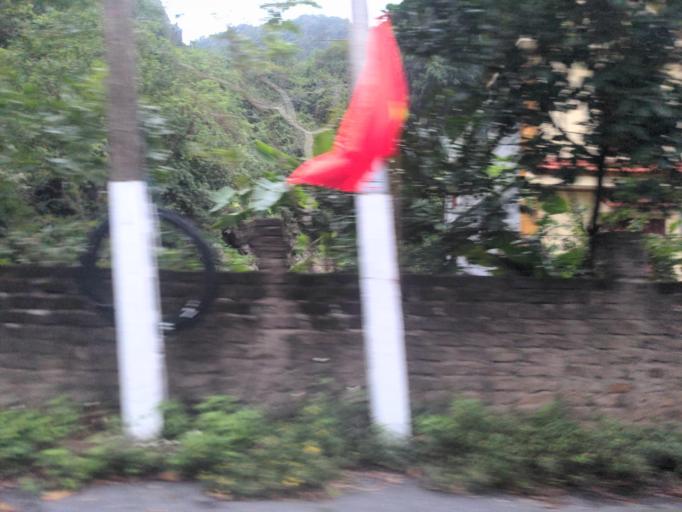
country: VN
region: Ninh Binh
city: Thi Tran Tam Diep
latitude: 20.2127
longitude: 105.9135
